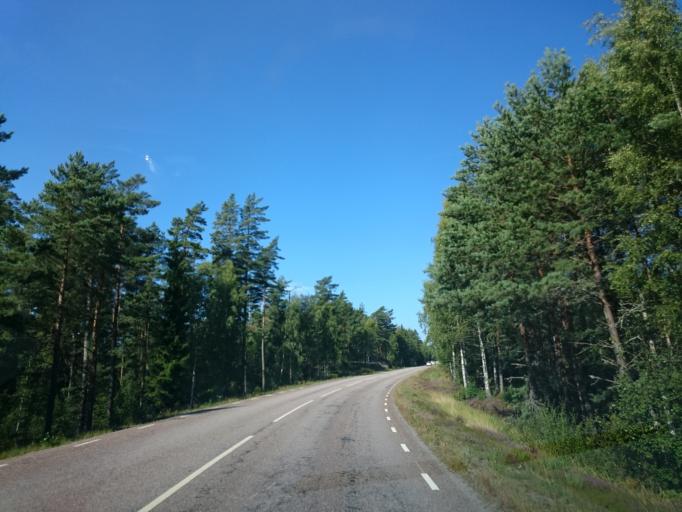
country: SE
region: OEstergoetland
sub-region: Norrkopings Kommun
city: Krokek
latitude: 58.6456
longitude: 16.5778
